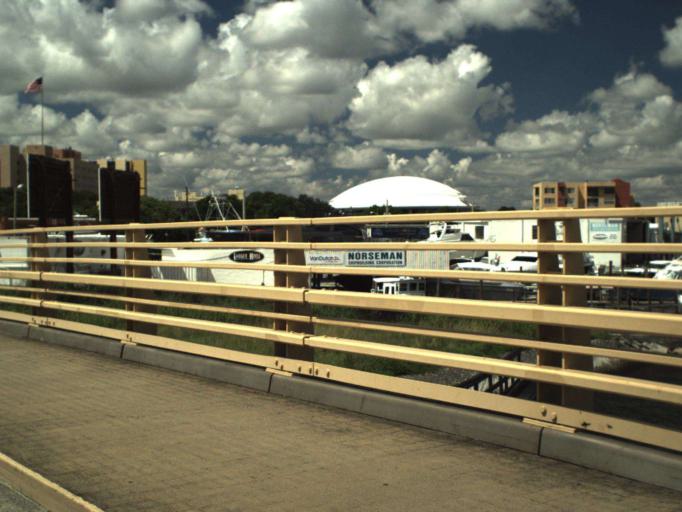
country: US
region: Florida
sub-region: Miami-Dade County
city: Miami
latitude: 25.7783
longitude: -80.2071
